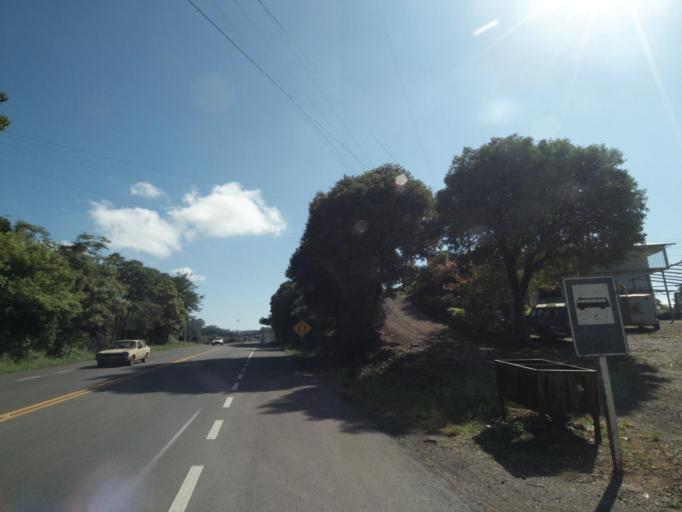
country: BR
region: Rio Grande do Sul
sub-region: Bento Goncalves
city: Bento Goncalves
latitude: -29.1215
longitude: -51.5437
